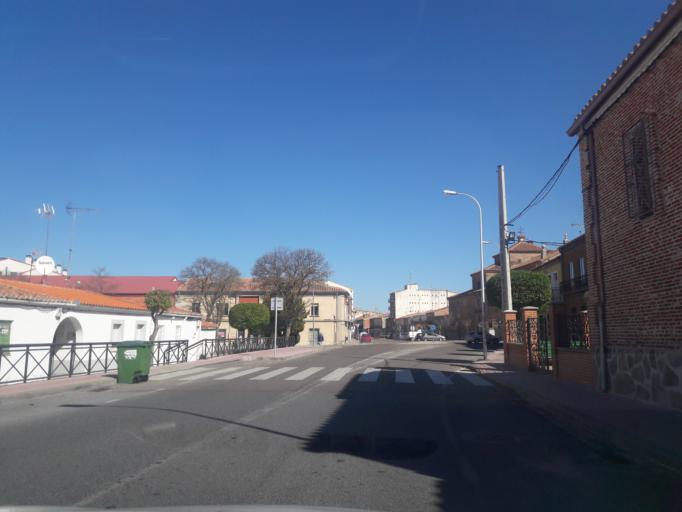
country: ES
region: Castille and Leon
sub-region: Provincia de Salamanca
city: Penaranda de Bracamonte
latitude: 40.8980
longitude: -5.2009
